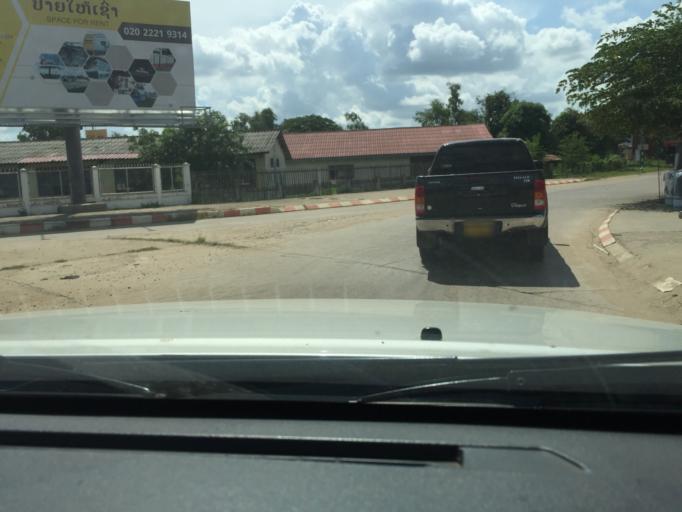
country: LA
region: Savannahkhet
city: Savannakhet
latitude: 16.5507
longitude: 104.7475
